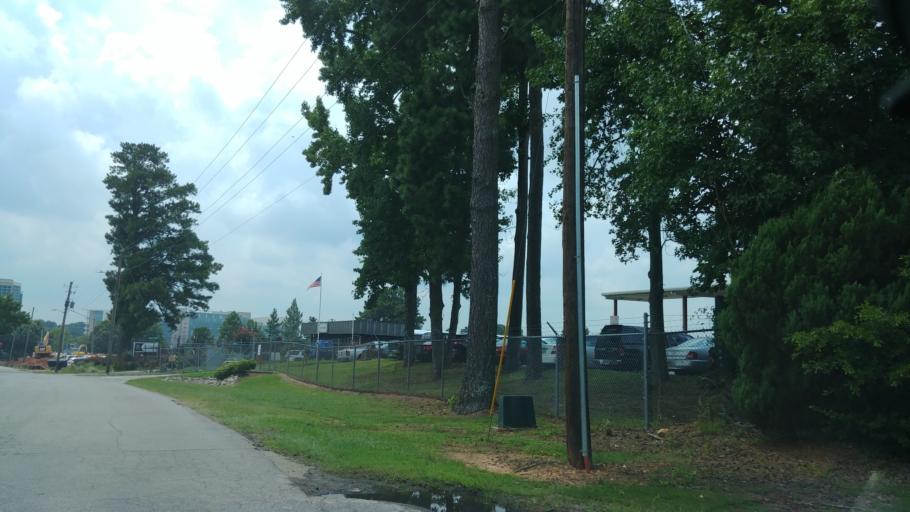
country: US
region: Georgia
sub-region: DeKalb County
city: Chamblee
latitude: 33.8880
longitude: -84.2917
